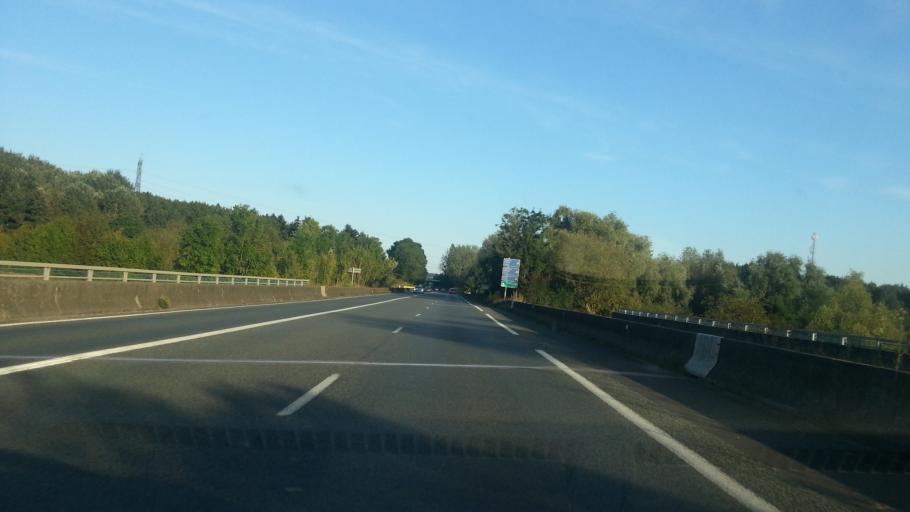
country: FR
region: Picardie
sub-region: Departement de l'Oise
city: Remy
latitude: 49.4019
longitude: 2.6932
